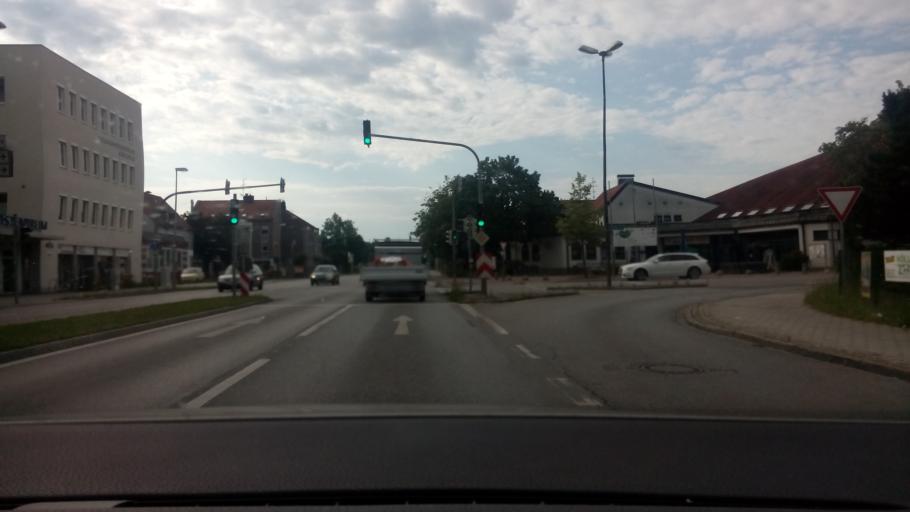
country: DE
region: Bavaria
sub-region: Upper Bavaria
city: Karlsfeld
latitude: 48.2238
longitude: 11.4703
